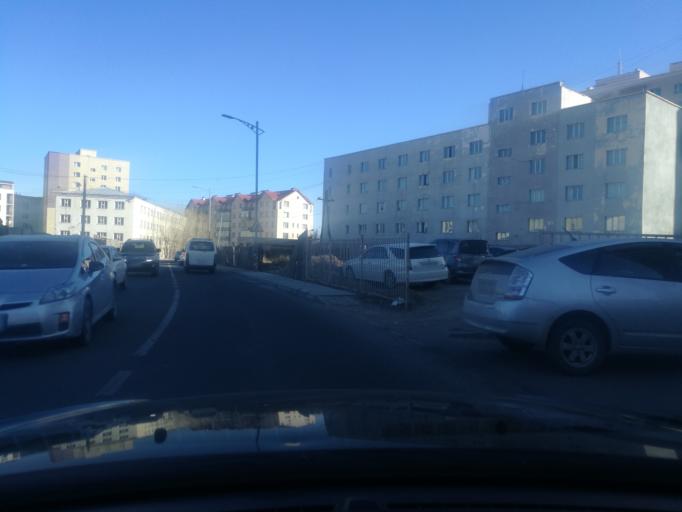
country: MN
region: Ulaanbaatar
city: Ulaanbaatar
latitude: 47.8863
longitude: 106.9048
